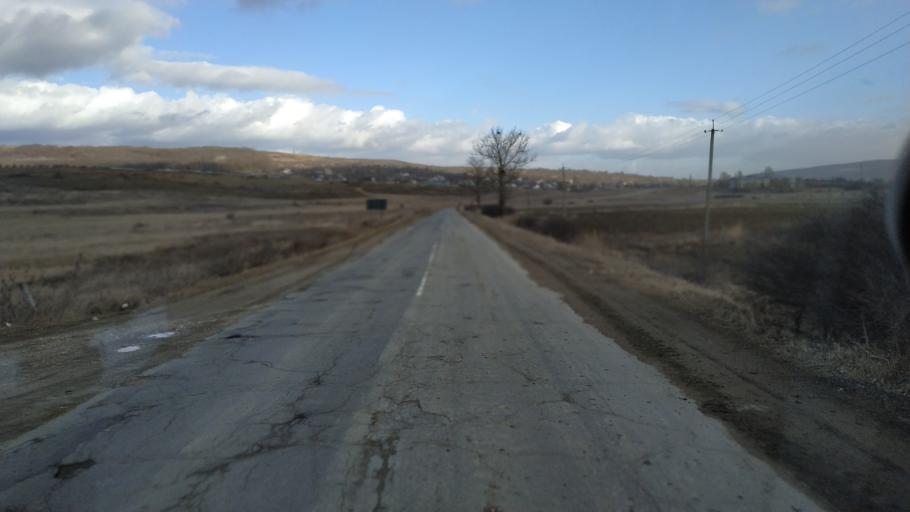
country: MD
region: Calarasi
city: Calarasi
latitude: 47.3280
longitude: 28.0958
